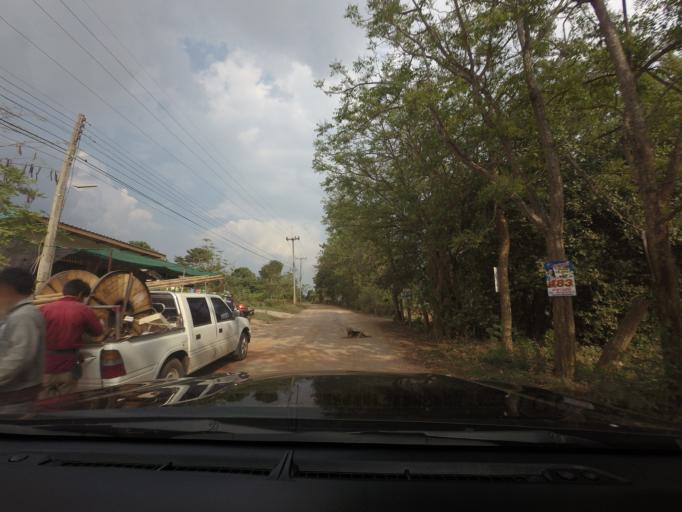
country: TH
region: Nakhon Ratchasima
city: Wang Nam Khiao
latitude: 14.4430
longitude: 101.6799
